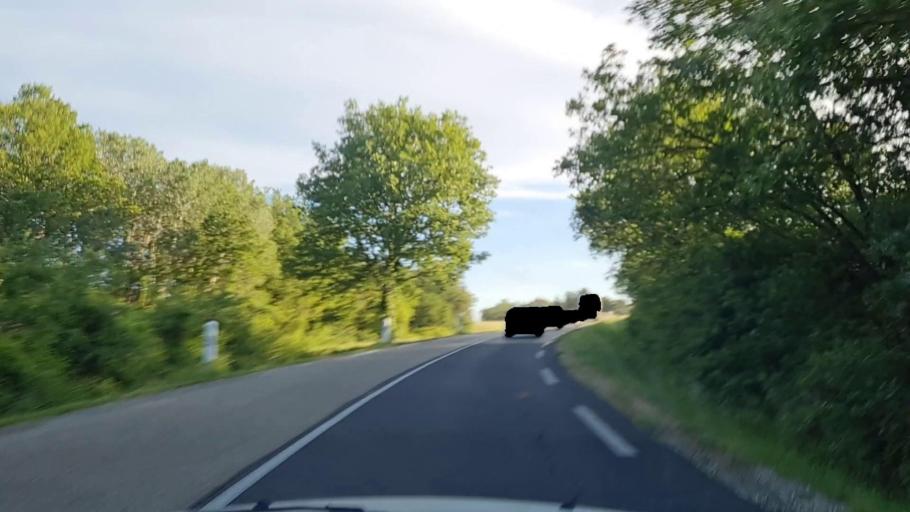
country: FR
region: Languedoc-Roussillon
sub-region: Departement du Gard
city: Ledignan
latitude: 43.9244
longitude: 4.1045
